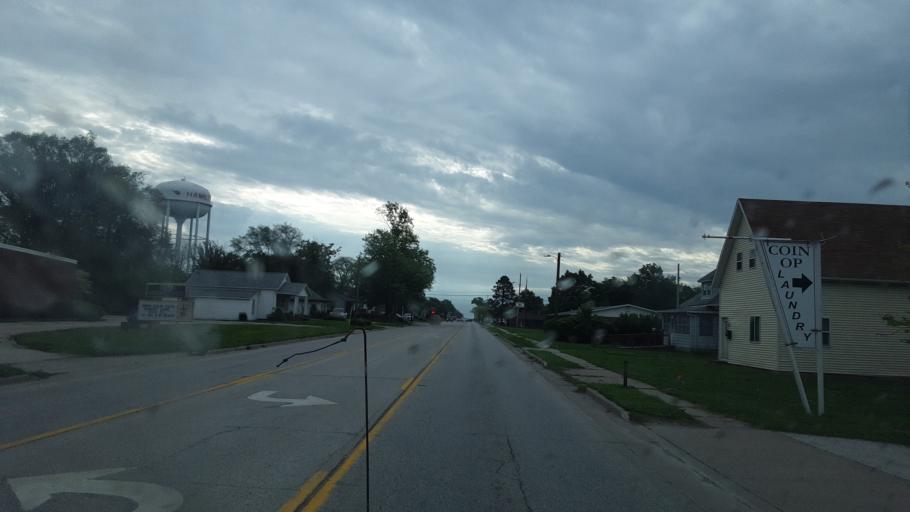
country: US
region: Illinois
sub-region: Hancock County
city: Hamilton
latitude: 40.3964
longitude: -91.3356
